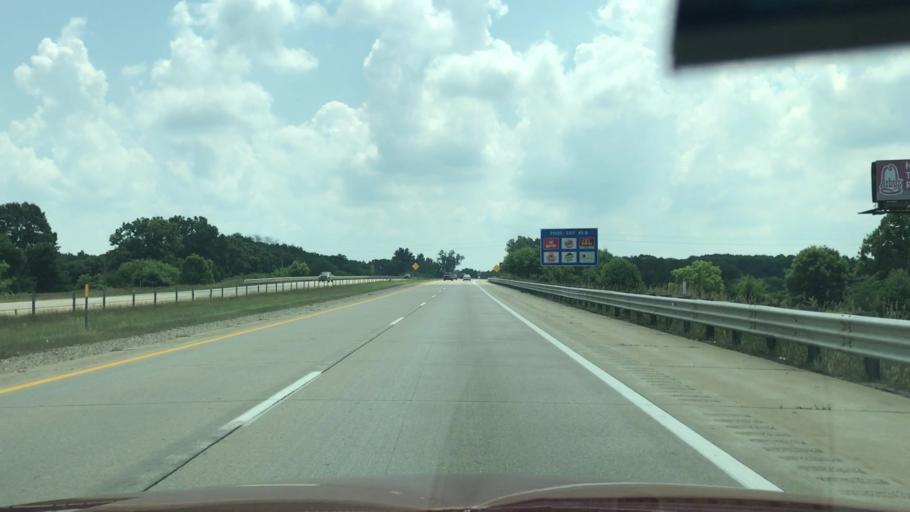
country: US
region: Michigan
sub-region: Allegan County
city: Plainwell
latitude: 42.4628
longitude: -85.6528
